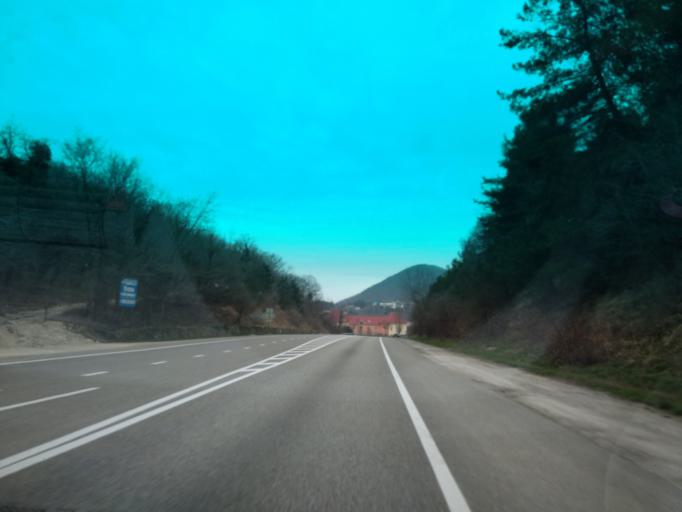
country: RU
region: Krasnodarskiy
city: Ol'ginka
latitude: 44.1892
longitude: 38.8902
